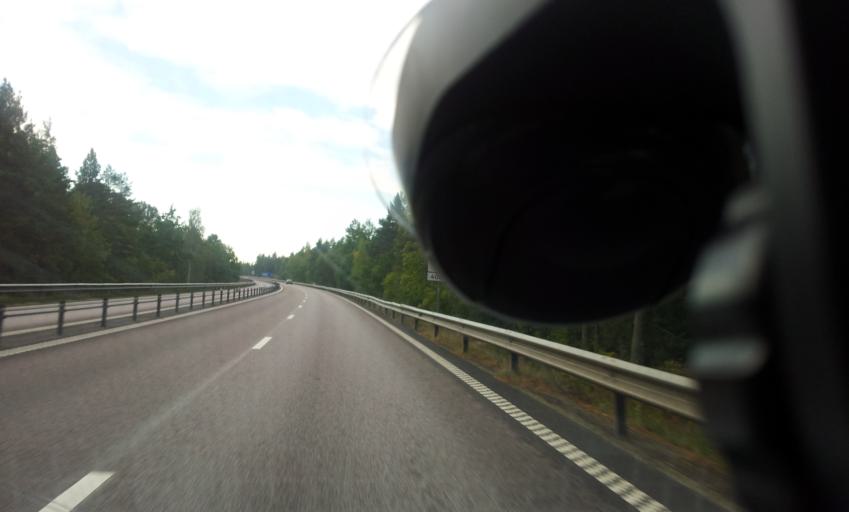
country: SE
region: Kalmar
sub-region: Oskarshamns Kommun
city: Oskarshamn
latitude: 57.2535
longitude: 16.4219
